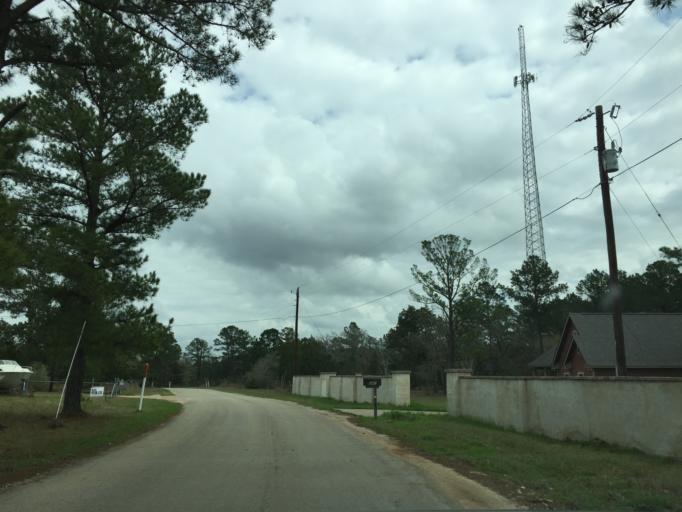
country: US
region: Texas
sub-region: Bastrop County
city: Bastrop
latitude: 30.1269
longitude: -97.2912
